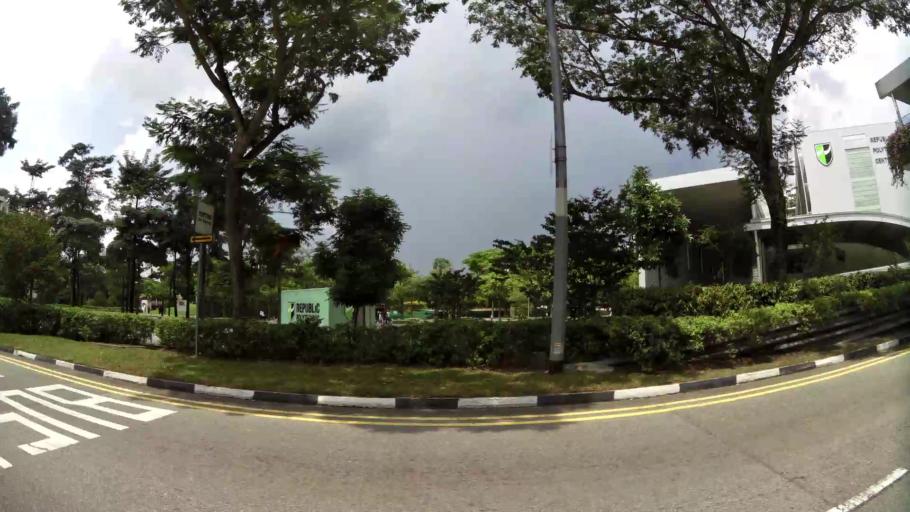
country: MY
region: Johor
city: Johor Bahru
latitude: 1.4419
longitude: 103.7855
